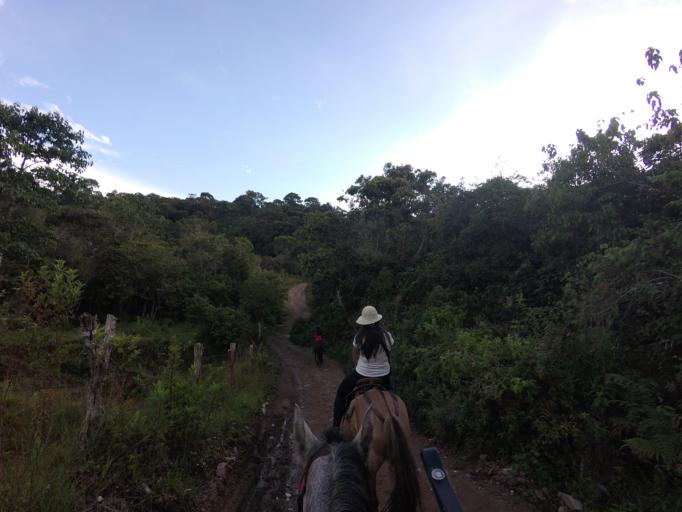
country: CO
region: Huila
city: San Agustin
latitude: 1.8989
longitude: -76.2731
